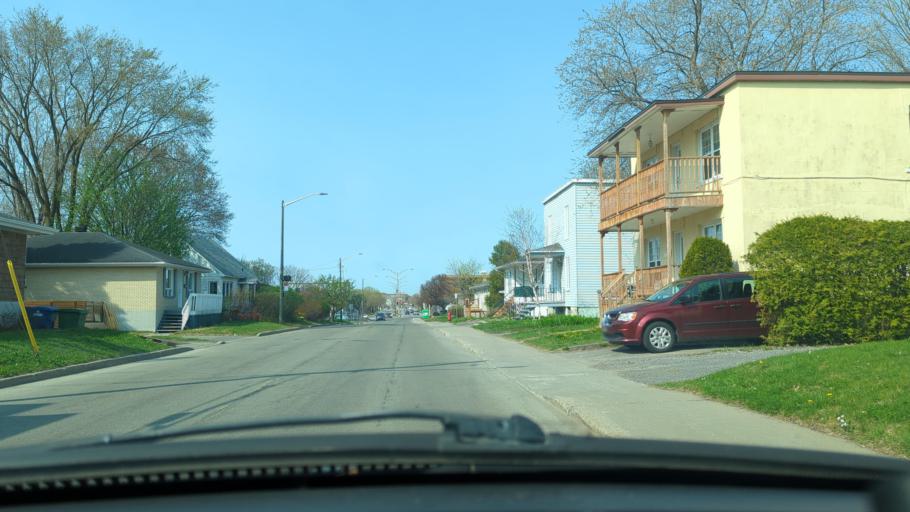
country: CA
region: Quebec
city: Quebec
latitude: 46.8484
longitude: -71.2575
